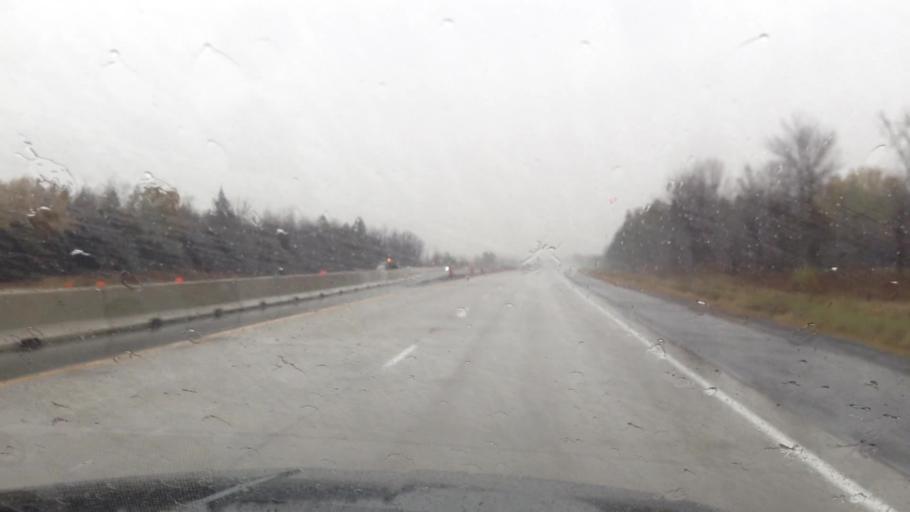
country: CA
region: Ontario
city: Hawkesbury
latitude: 45.5055
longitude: -74.5849
